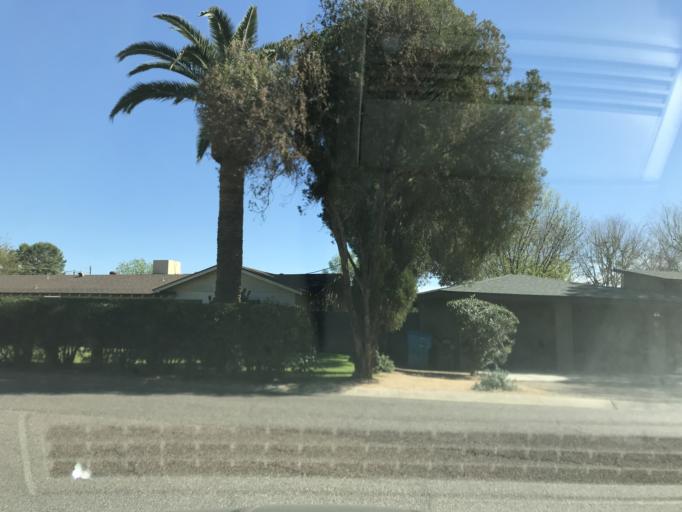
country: US
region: Arizona
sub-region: Maricopa County
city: Phoenix
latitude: 33.5215
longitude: -112.0879
